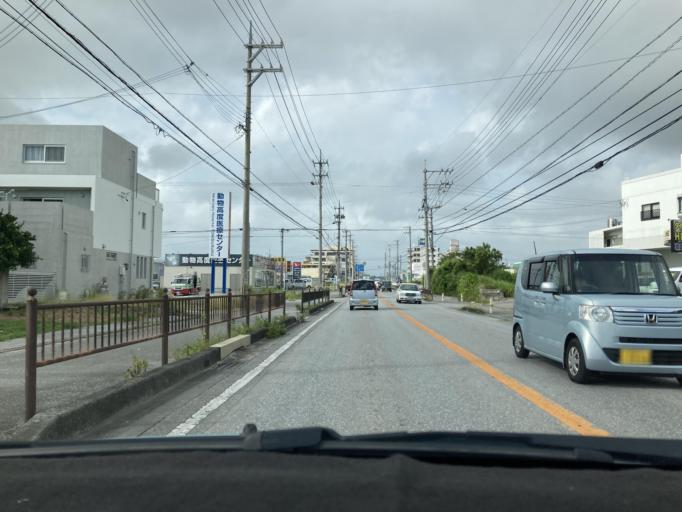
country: JP
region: Okinawa
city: Tomigusuku
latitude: 26.1579
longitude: 127.6704
